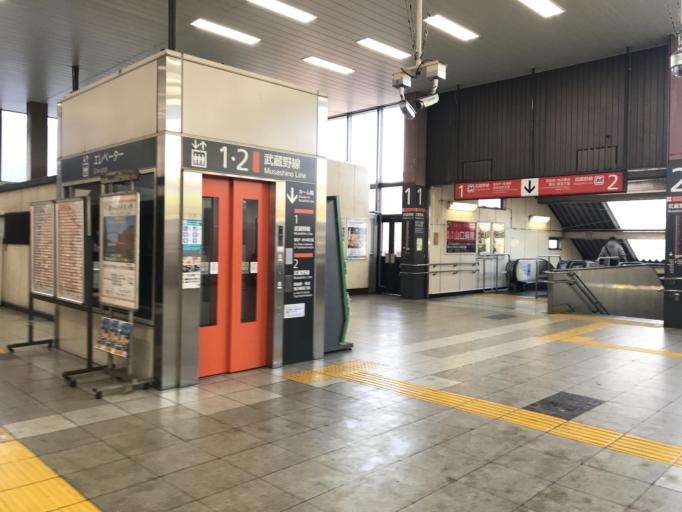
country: JP
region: Chiba
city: Funabashi
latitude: 35.7309
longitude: 139.9666
